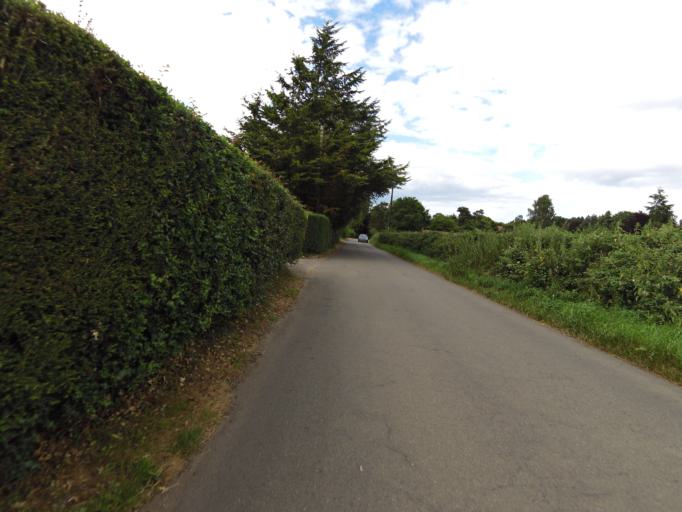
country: GB
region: England
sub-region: Suffolk
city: Beccles
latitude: 52.4717
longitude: 1.5138
